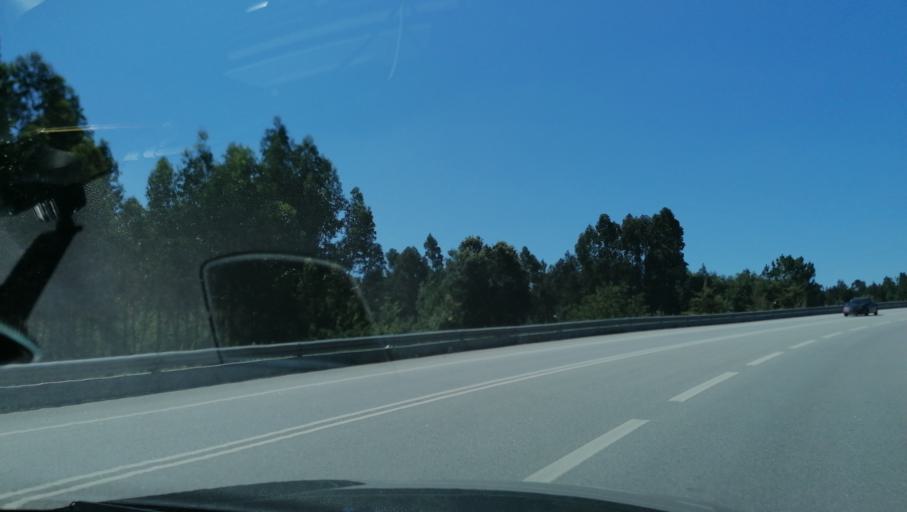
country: PT
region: Aveiro
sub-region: Agueda
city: Agueda
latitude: 40.5586
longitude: -8.4563
